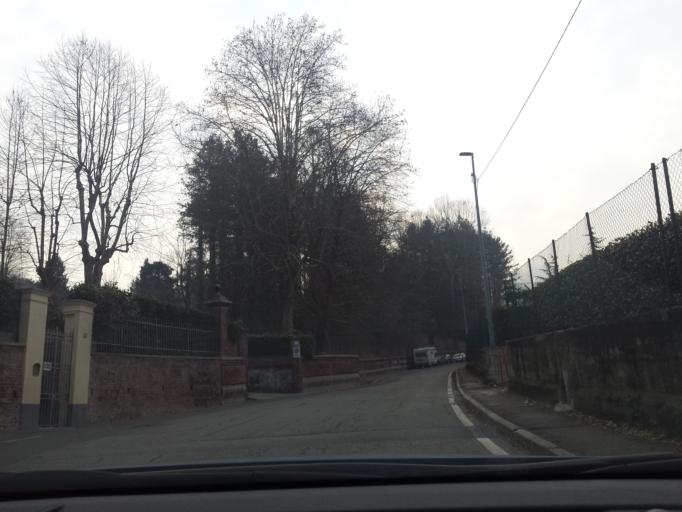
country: IT
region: Piedmont
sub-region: Provincia di Torino
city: Turin
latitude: 45.0607
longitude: 7.7163
